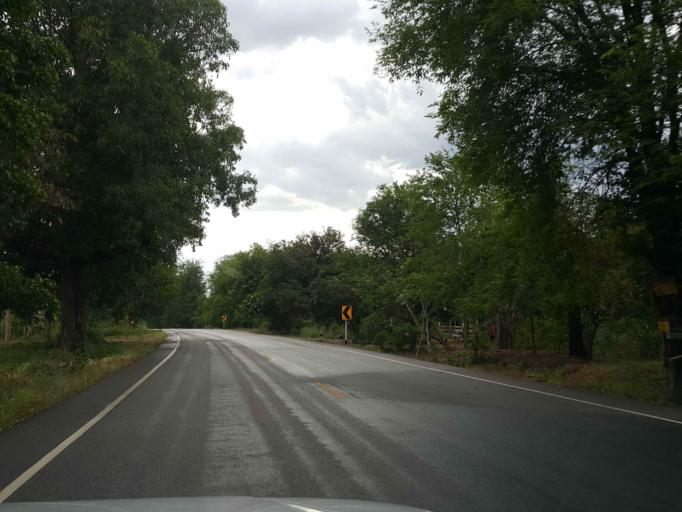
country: TH
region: Lampang
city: Thoen
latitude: 17.6517
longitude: 99.2596
